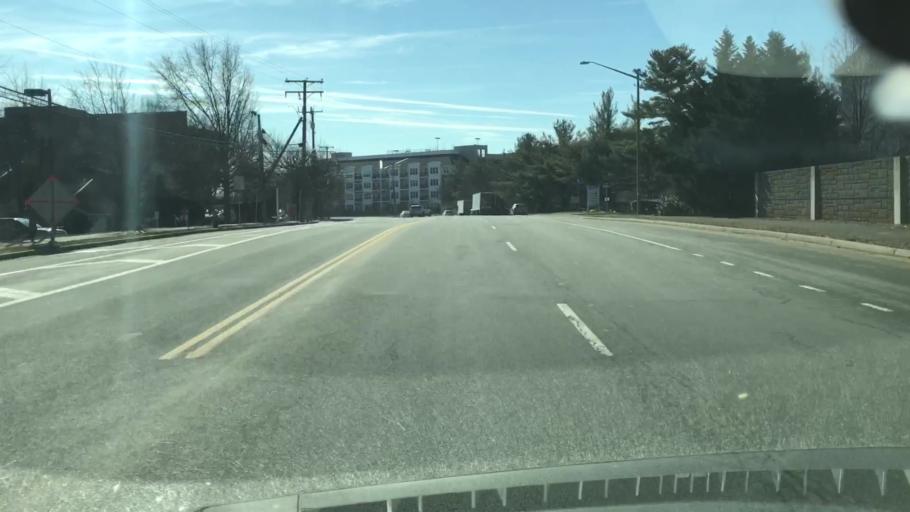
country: US
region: Virginia
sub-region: City of Fairfax
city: Fairfax
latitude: 38.8630
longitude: -77.3363
